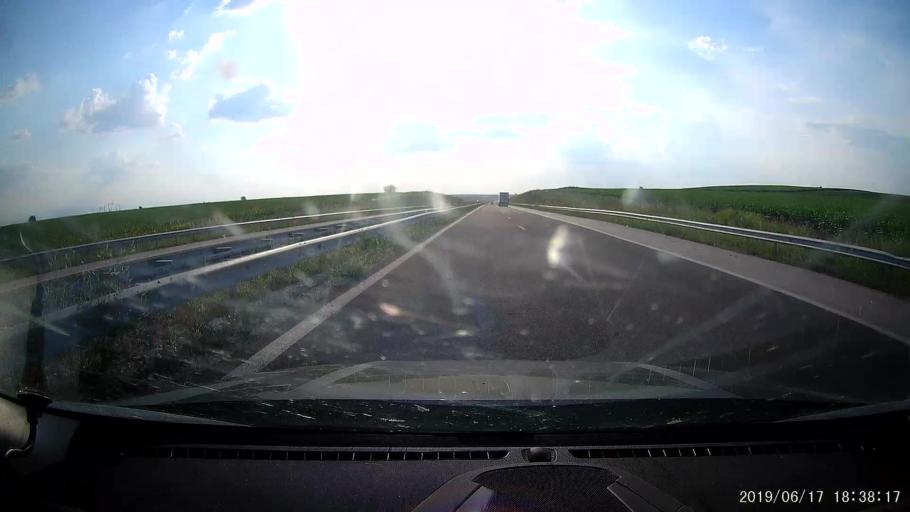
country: BG
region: Stara Zagora
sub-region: Obshtina Chirpan
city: Chirpan
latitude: 42.1360
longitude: 25.3412
